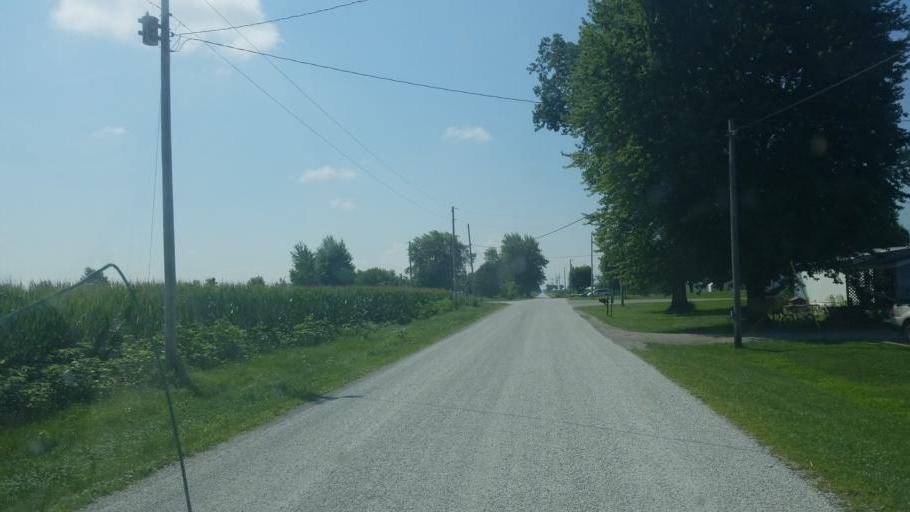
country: US
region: Ohio
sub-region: Hardin County
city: Kenton
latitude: 40.6775
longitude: -83.7293
